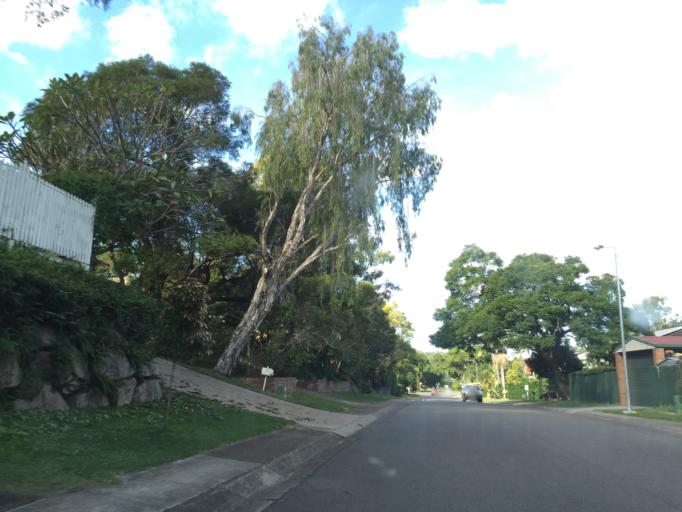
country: AU
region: Queensland
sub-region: Moreton Bay
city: Ferny Hills
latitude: -27.4374
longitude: 152.9331
